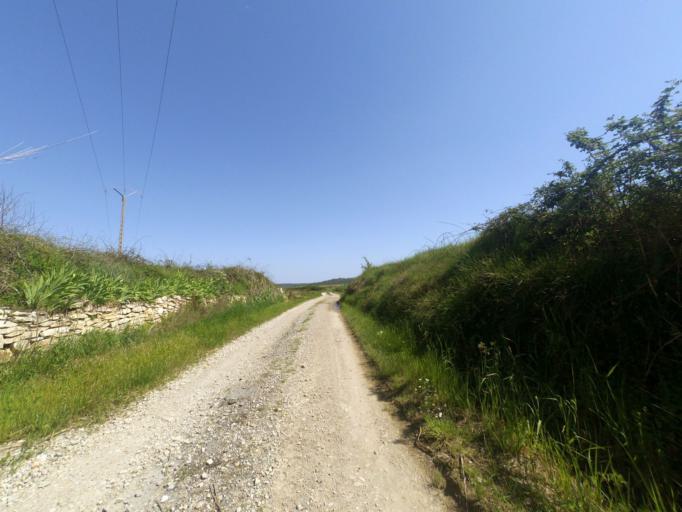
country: FR
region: Languedoc-Roussillon
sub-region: Departement du Gard
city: Congenies
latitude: 43.7727
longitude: 4.1720
